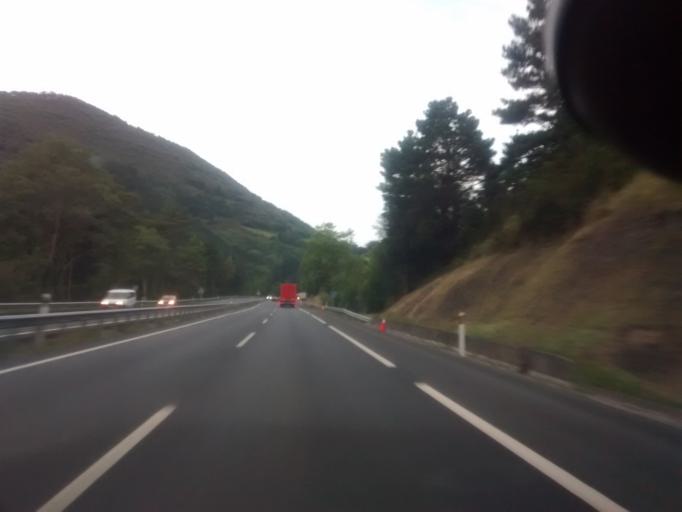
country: ES
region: Basque Country
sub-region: Provincia de Guipuzcoa
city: Deba
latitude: 43.2694
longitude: -2.3041
